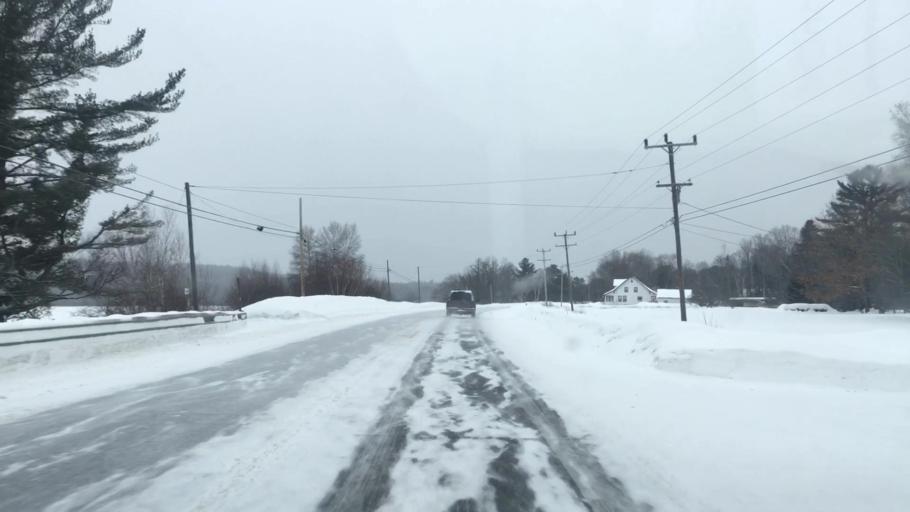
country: US
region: Maine
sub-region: Penobscot County
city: Medway
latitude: 45.5952
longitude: -68.4888
